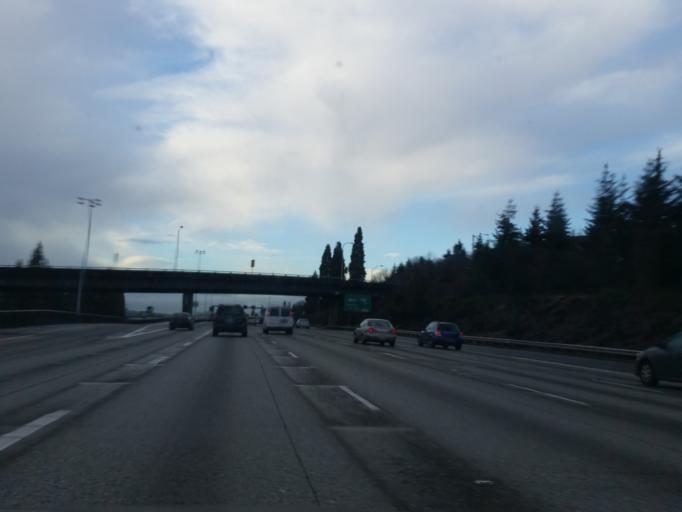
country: US
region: Washington
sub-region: King County
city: White Center
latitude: 47.5488
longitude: -122.3122
